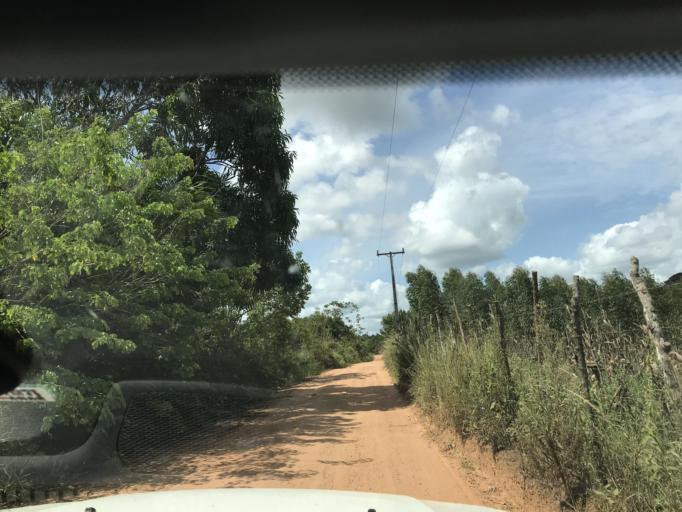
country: BR
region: Bahia
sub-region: Entre Rios
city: Entre Rios
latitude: -12.2196
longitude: -38.0836
